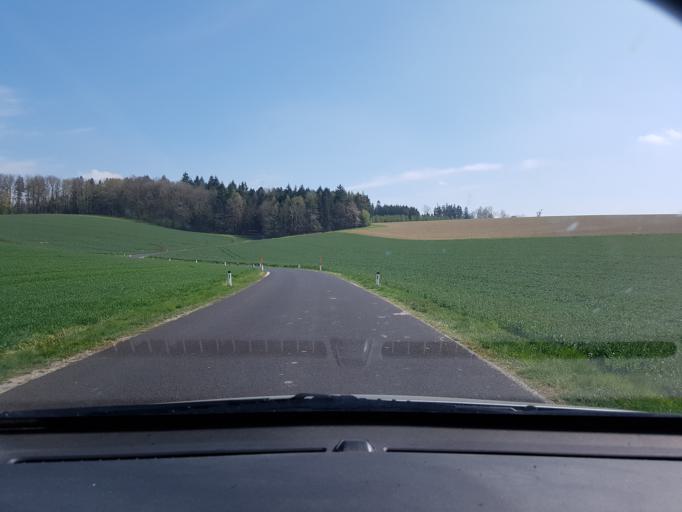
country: AT
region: Upper Austria
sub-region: Politischer Bezirk Linz-Land
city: Ansfelden
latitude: 48.2001
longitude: 14.3185
